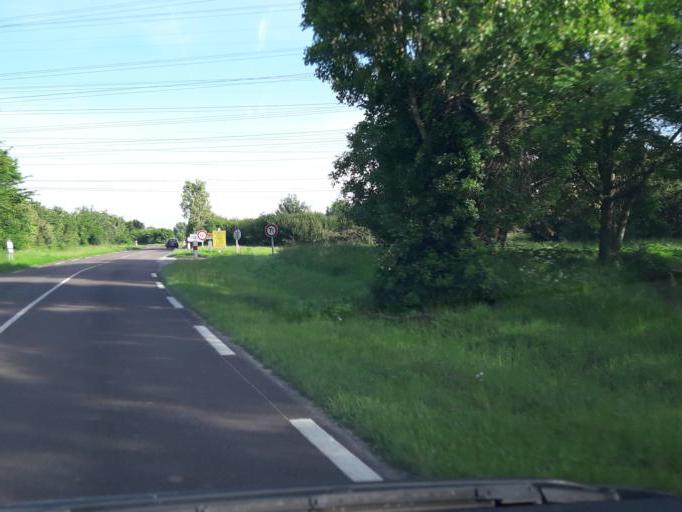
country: FR
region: Ile-de-France
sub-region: Departement de l'Essonne
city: Saint-Vrain
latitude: 48.5501
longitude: 2.3168
